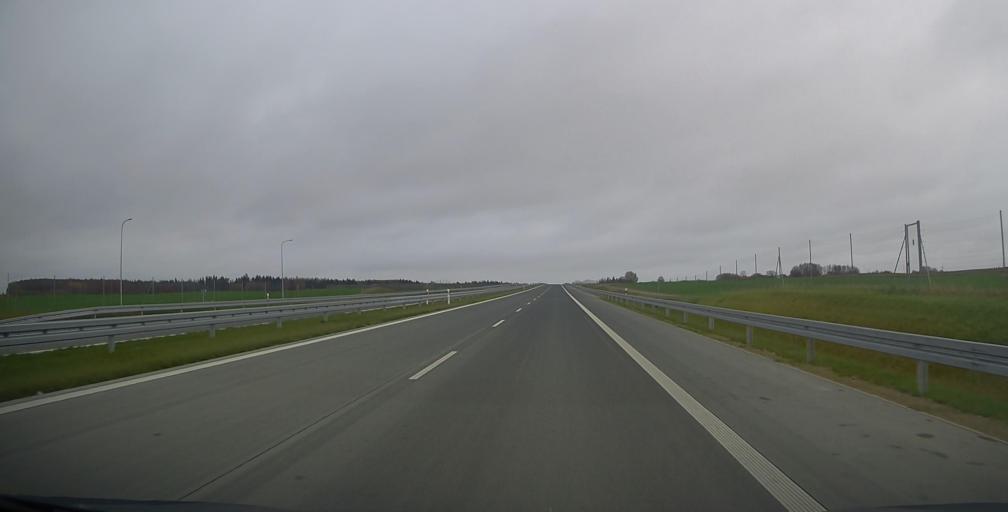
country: PL
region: Podlasie
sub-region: Powiat suwalski
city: Raczki
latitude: 53.8841
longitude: 22.6698
